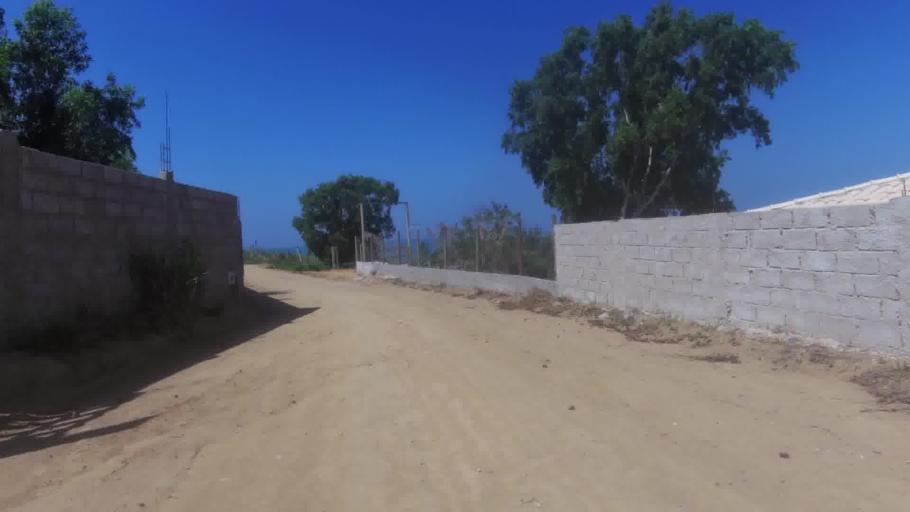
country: BR
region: Espirito Santo
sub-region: Marataizes
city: Marataizes
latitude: -21.1113
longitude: -40.8570
